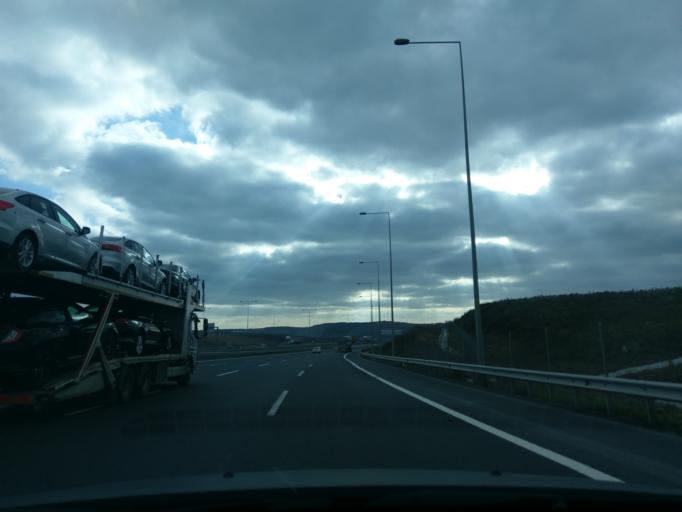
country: TR
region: Istanbul
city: Kemerburgaz
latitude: 41.2283
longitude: 28.8418
